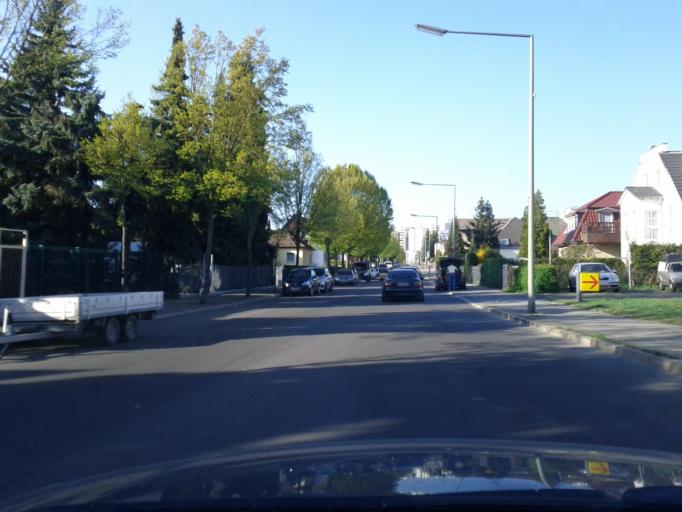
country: DE
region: Berlin
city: Markisches Viertel
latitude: 52.5918
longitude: 13.3462
